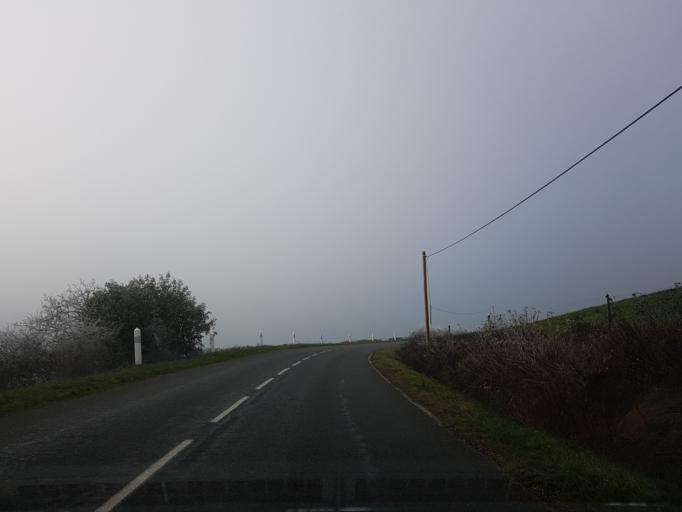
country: FR
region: Bourgogne
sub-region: Departement de Saone-et-Loire
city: Saint-Berain-sous-Sanvignes
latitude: 46.7281
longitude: 4.2925
